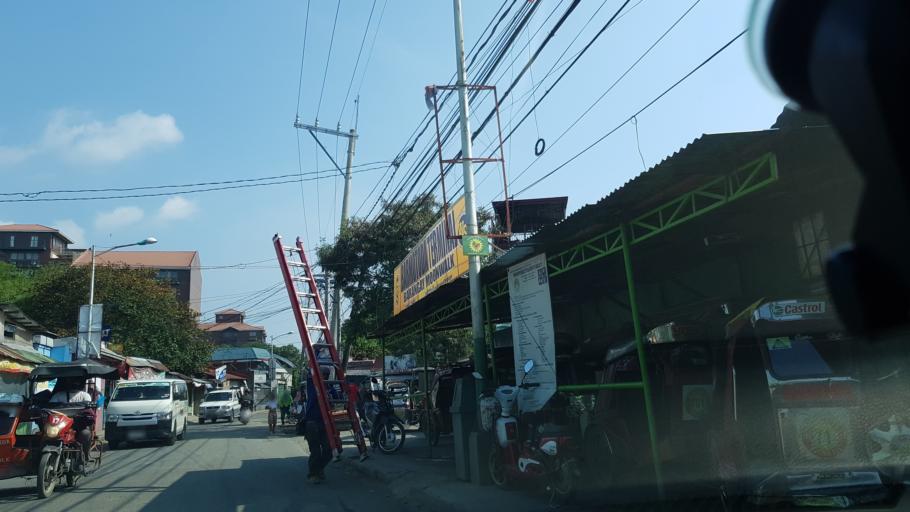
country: PH
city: Sambayanihan People's Village
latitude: 14.4970
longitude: 121.0134
